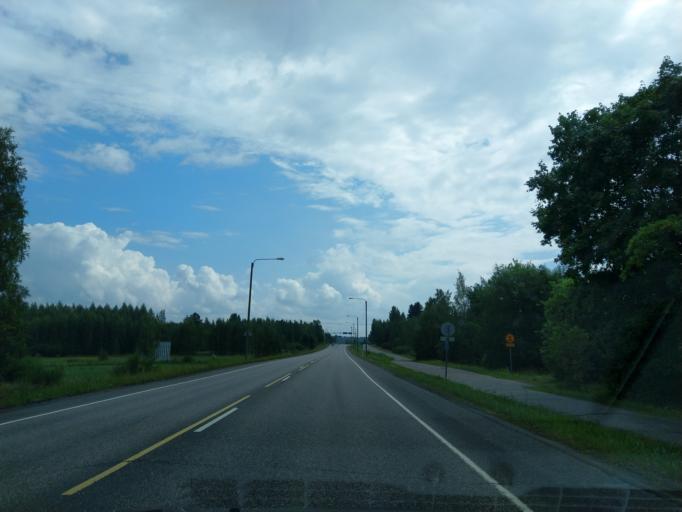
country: FI
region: South Karelia
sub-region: Imatra
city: Parikkala
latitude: 61.5900
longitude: 29.4898
